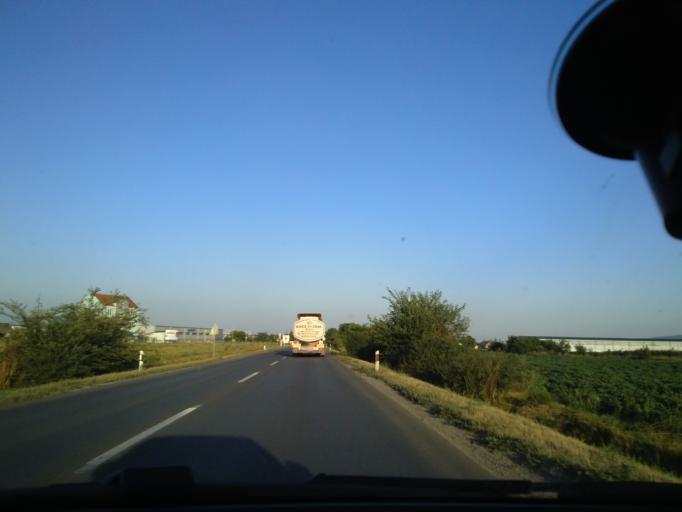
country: RS
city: Rumenka
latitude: 45.2854
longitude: 19.7628
